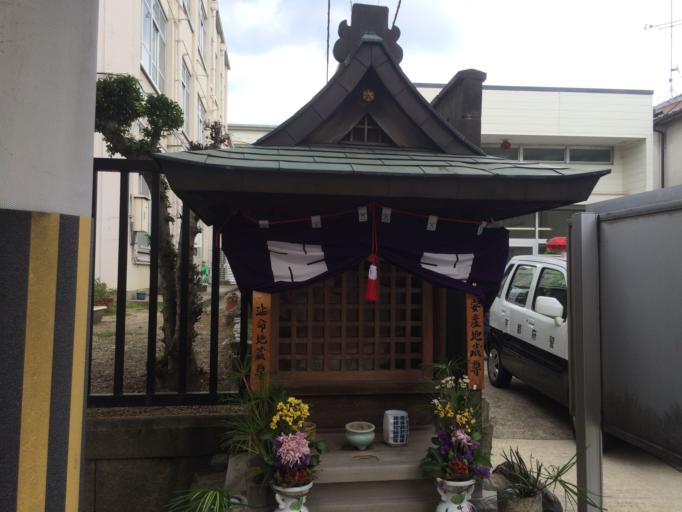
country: JP
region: Kyoto
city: Kyoto
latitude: 34.9560
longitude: 135.7713
